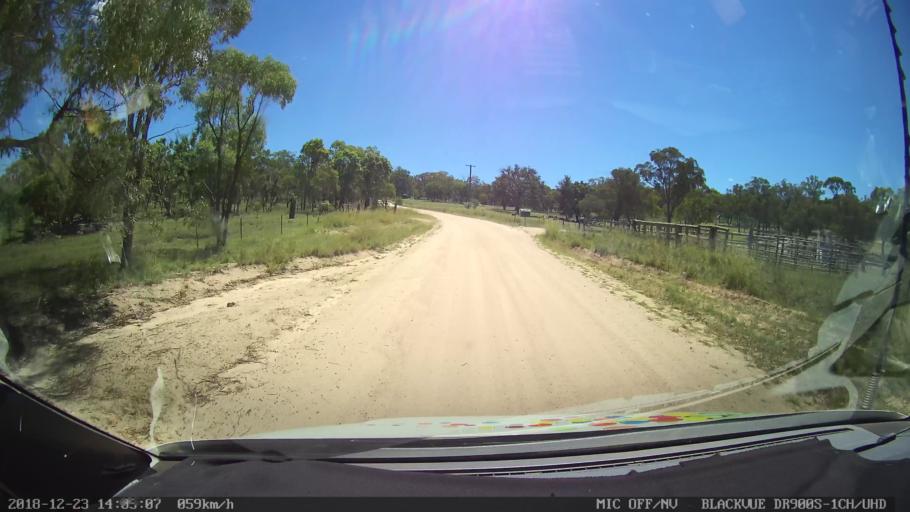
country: AU
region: New South Wales
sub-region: Tamworth Municipality
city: Manilla
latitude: -30.6239
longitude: 151.0835
